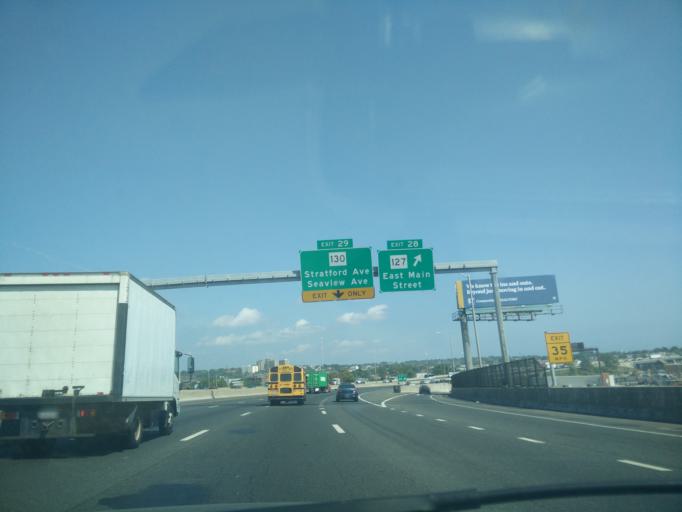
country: US
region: Connecticut
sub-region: Fairfield County
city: Bridgeport
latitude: 41.1779
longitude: -73.1845
